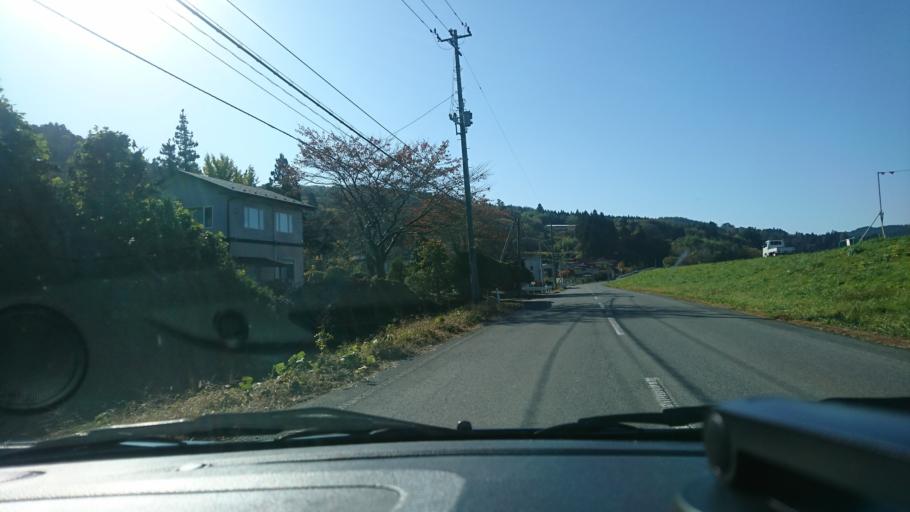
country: JP
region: Iwate
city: Ichinoseki
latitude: 38.8360
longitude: 141.2679
